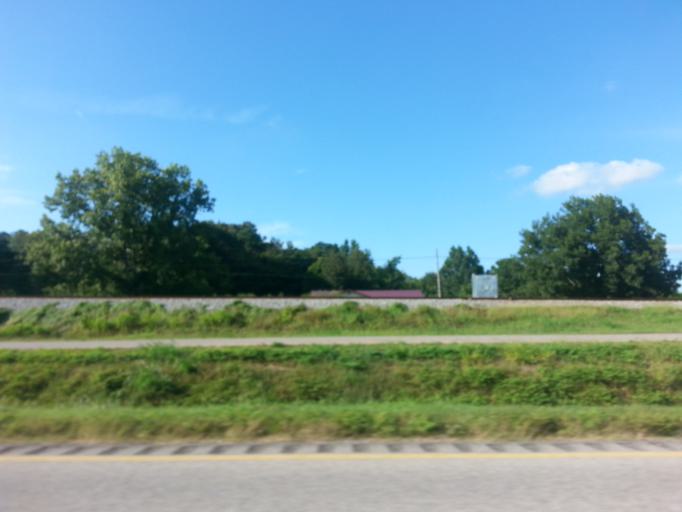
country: US
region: Alabama
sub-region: Colbert County
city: Tuscumbia
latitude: 34.7099
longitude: -87.7634
